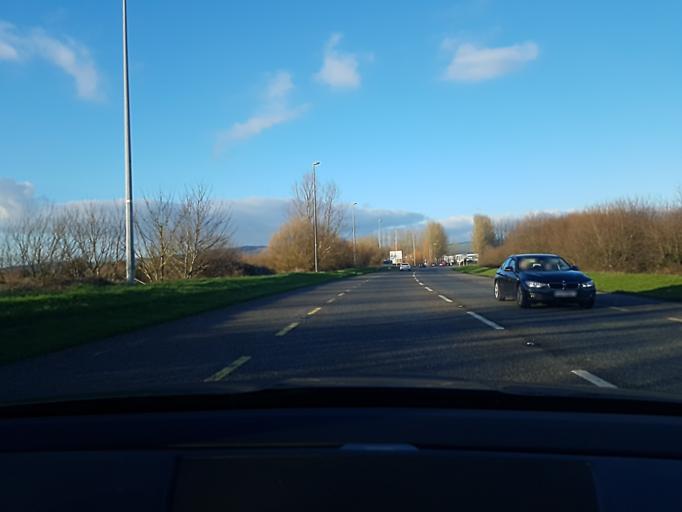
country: IE
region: Munster
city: Moyross
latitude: 52.6709
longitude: -8.6750
